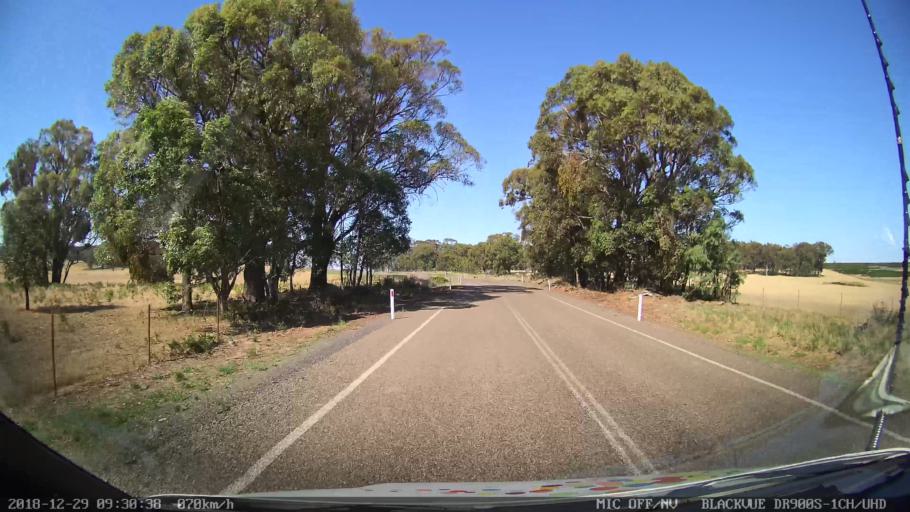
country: AU
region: New South Wales
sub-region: Upper Lachlan Shire
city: Crookwell
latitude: -34.6002
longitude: 149.3675
